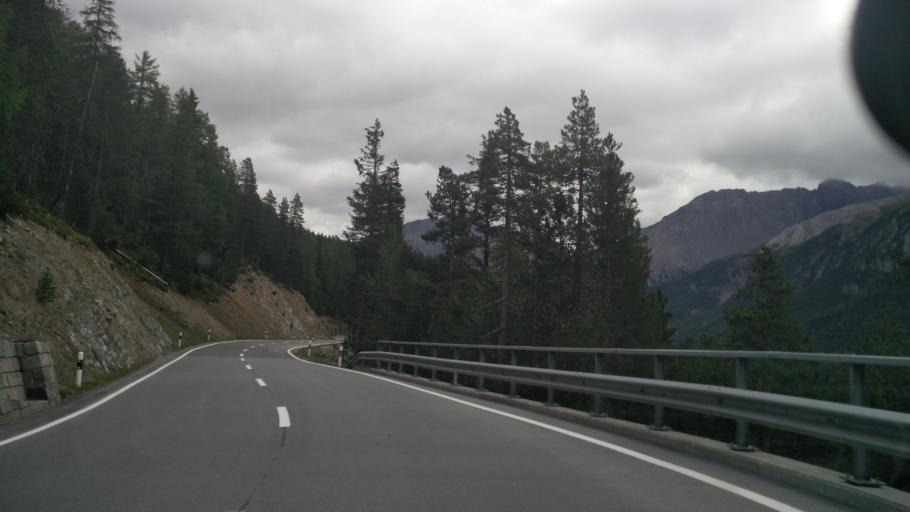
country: CH
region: Grisons
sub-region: Inn District
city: Zernez
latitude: 46.6777
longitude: 10.1646
